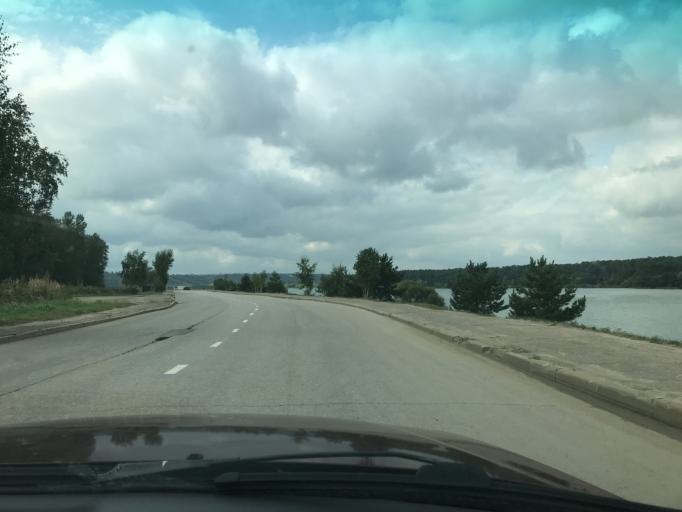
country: RU
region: Kaluga
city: Kaluga
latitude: 54.5201
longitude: 36.2314
